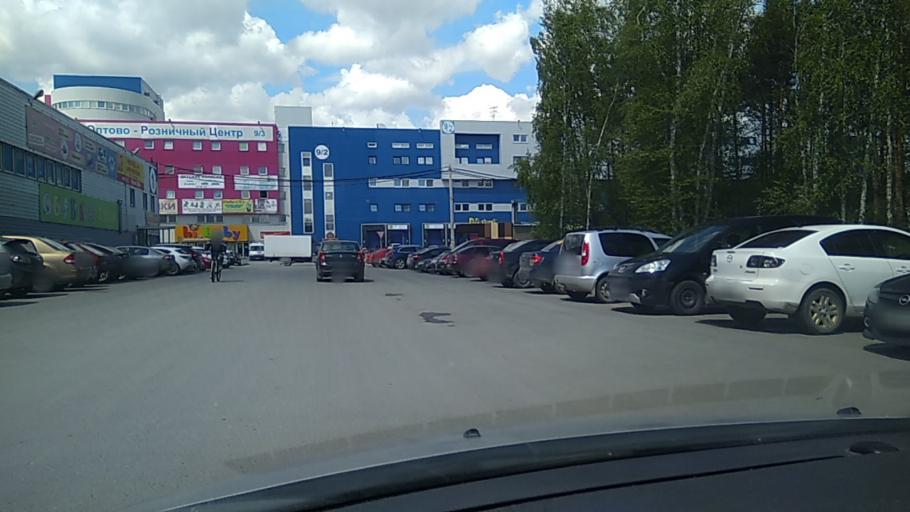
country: RU
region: Sverdlovsk
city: Istok
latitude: 56.7568
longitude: 60.7580
